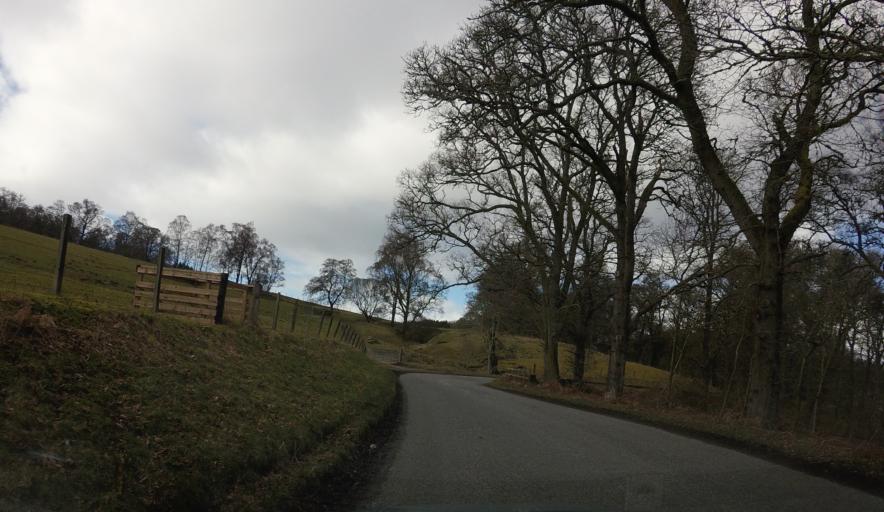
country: GB
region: Scotland
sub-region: Perth and Kinross
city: Pitlochry
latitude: 56.6416
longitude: -3.6762
